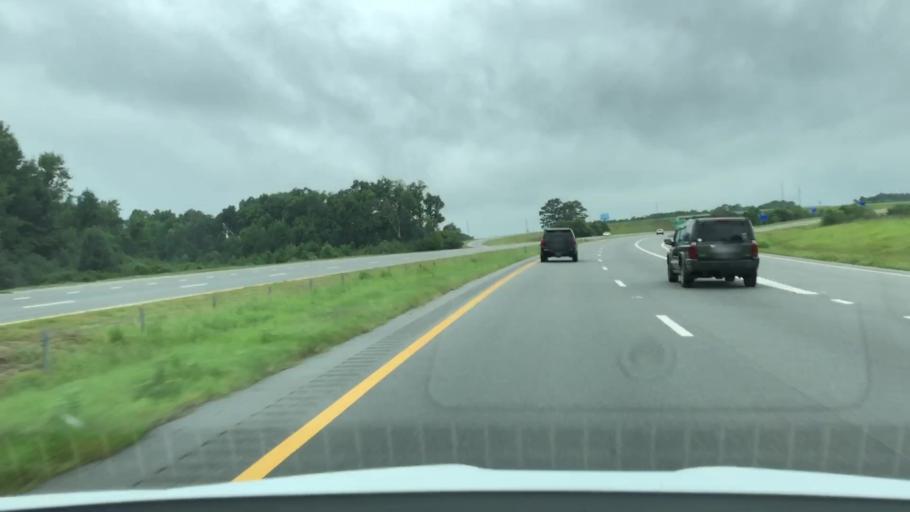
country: US
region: North Carolina
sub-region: Wayne County
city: Goldsboro
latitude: 35.4179
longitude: -77.9295
